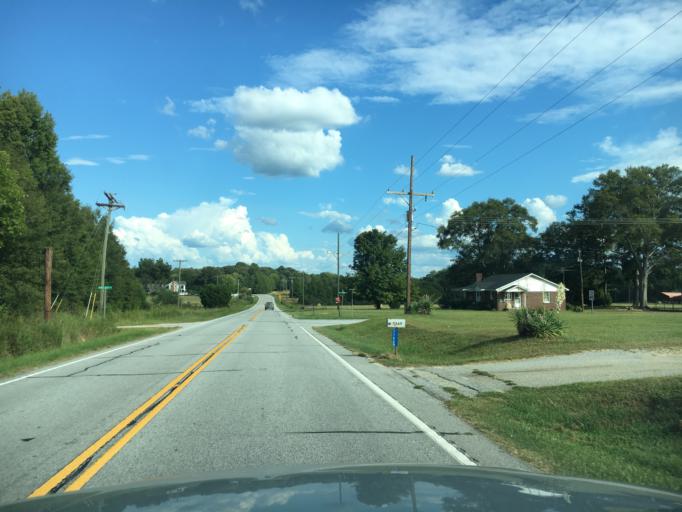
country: US
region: South Carolina
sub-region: Greenwood County
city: Ware Shoals
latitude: 34.5187
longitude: -82.1673
